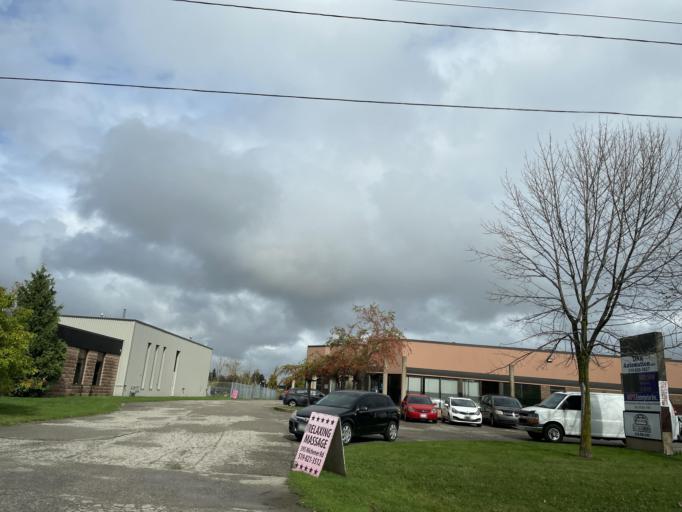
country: CA
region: Ontario
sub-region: Wellington County
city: Guelph
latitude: 43.5330
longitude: -80.3178
